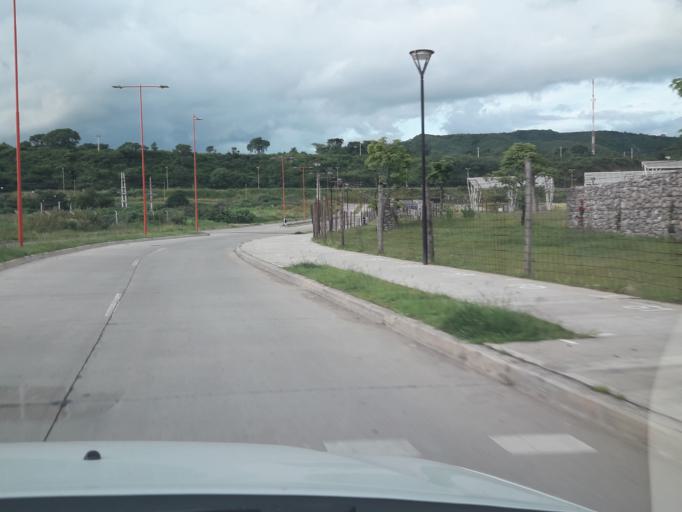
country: AR
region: Jujuy
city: San Salvador de Jujuy
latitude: -24.1827
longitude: -65.3283
